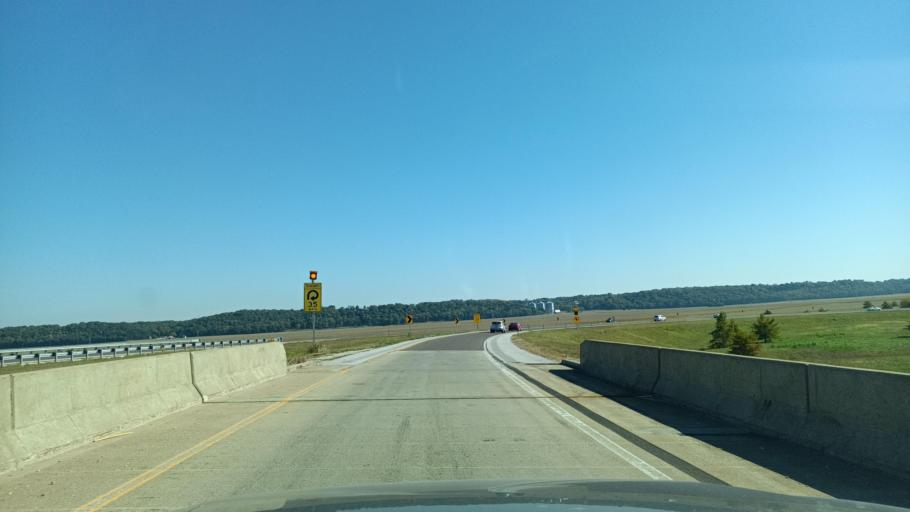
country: US
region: Missouri
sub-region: Marion County
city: Hannibal
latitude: 39.7555
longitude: -91.2982
